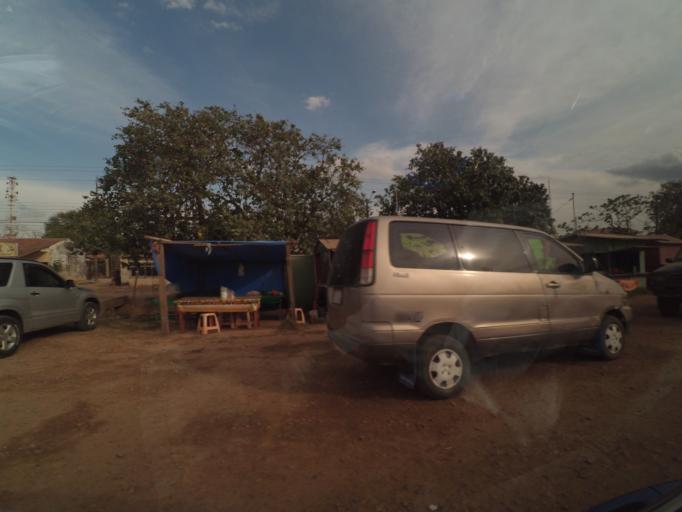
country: BO
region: Santa Cruz
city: Okinawa Numero Uno
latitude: -17.2200
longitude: -62.8949
